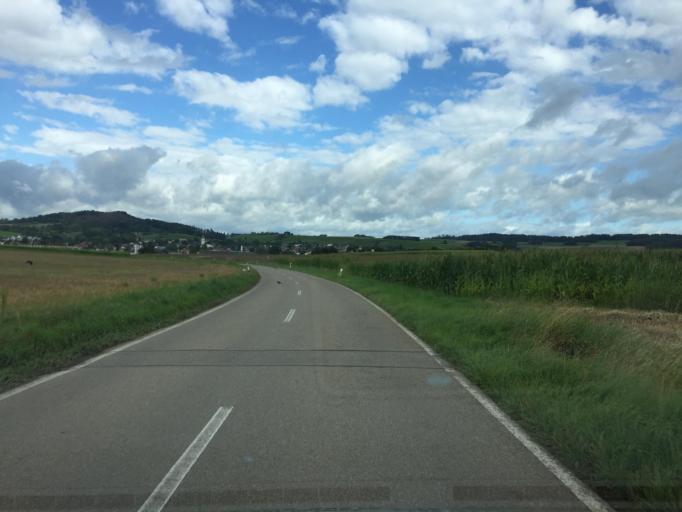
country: CH
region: Schaffhausen
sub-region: Bezirk Unterklettgau
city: Wilchingen
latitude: 47.6557
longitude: 8.4415
